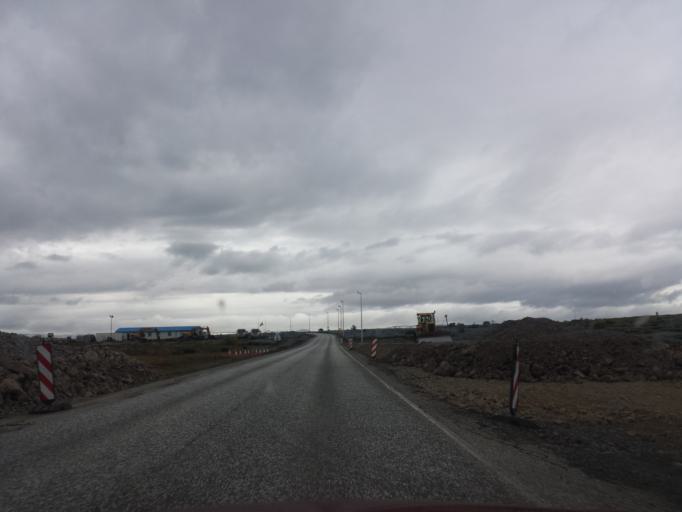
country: IS
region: Capital Region
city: Alftanes
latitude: 64.0916
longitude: -21.9883
